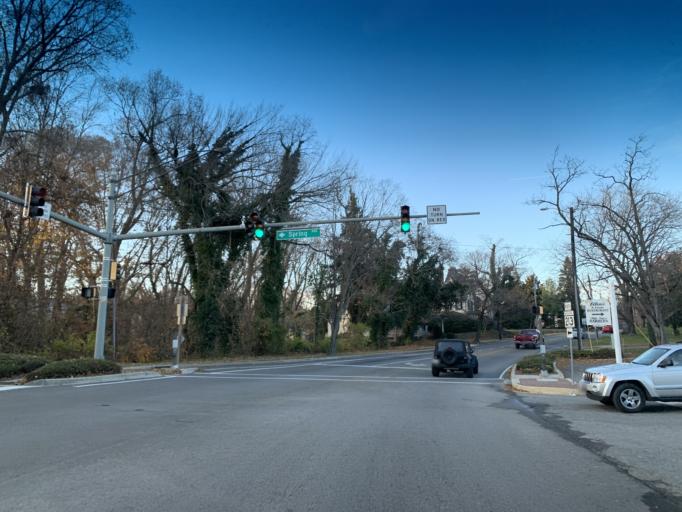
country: US
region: Maryland
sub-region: Kent County
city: Chestertown
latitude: 39.2112
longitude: -76.0656
